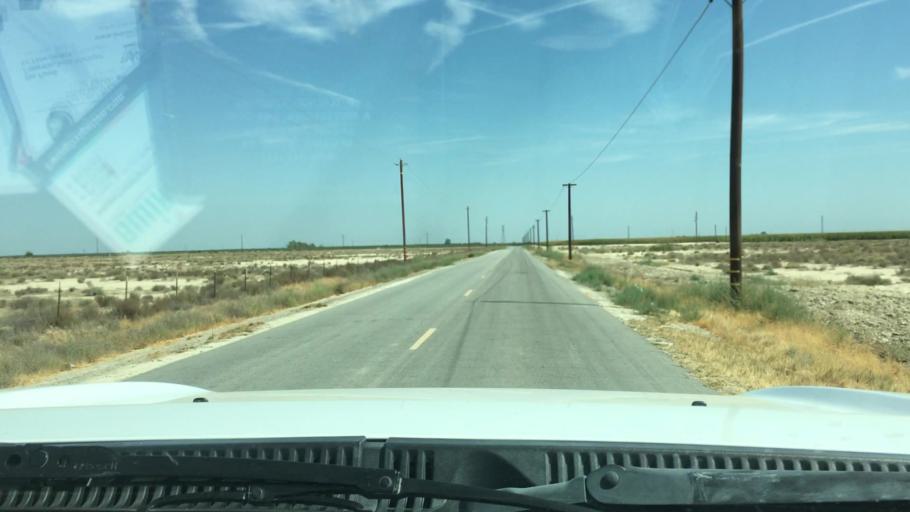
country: US
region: California
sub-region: Kern County
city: Buttonwillow
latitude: 35.4323
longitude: -119.3761
